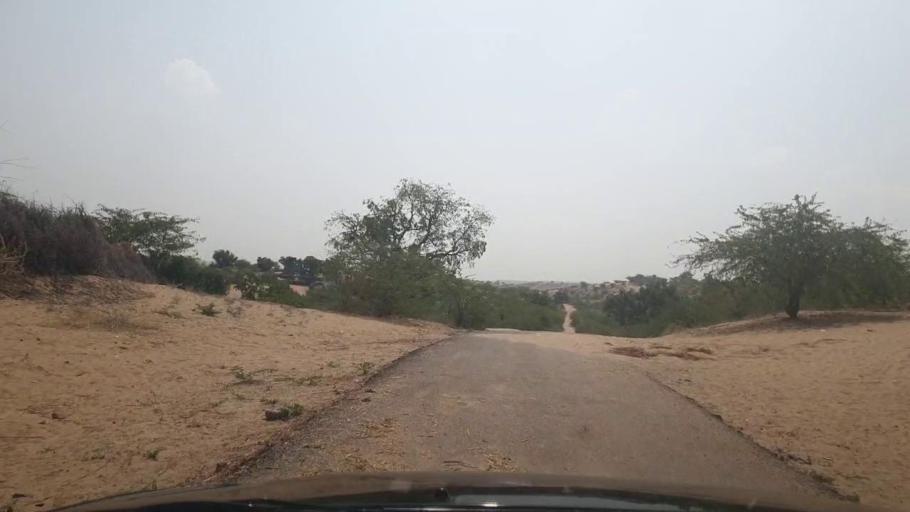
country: PK
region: Sindh
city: Islamkot
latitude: 25.0039
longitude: 70.4164
